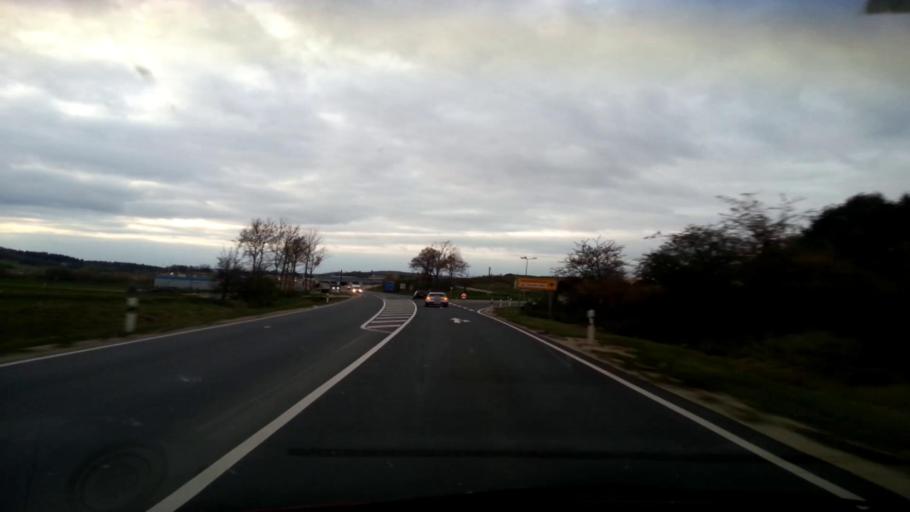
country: DE
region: Bavaria
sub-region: Upper Franconia
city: Niederfullbach
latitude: 50.2210
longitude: 11.0569
